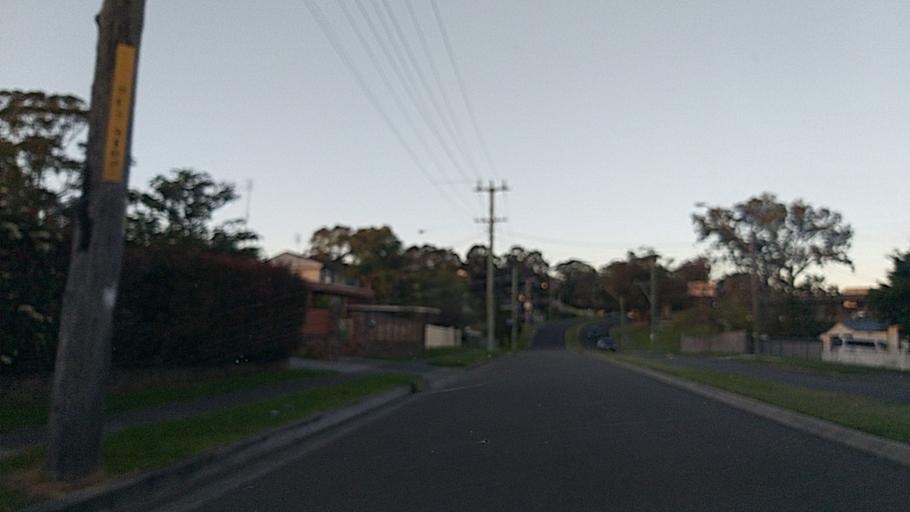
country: AU
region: New South Wales
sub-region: Wollongong
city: Koonawarra
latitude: -34.5039
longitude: 150.8032
